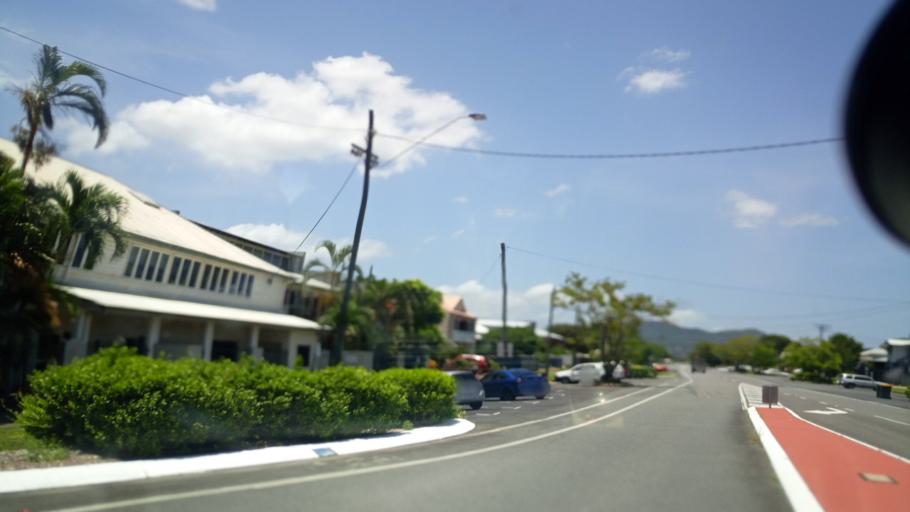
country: AU
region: Queensland
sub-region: Cairns
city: Cairns
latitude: -16.9290
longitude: 145.7706
